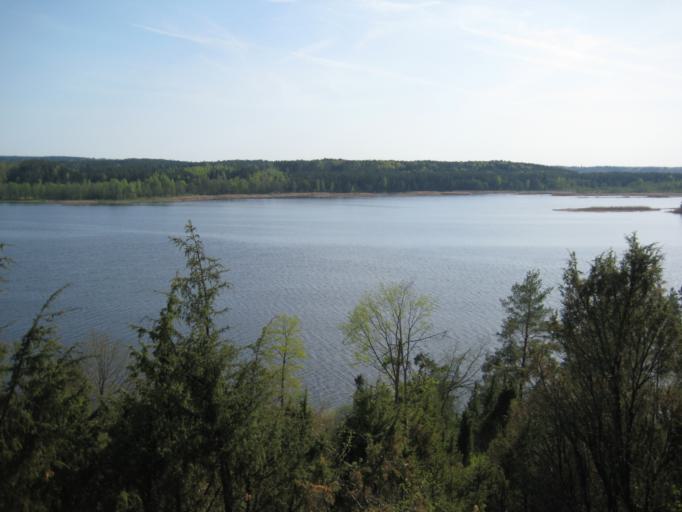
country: LT
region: Kauno apskritis
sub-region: Kauno rajonas
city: Karmelava
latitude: 54.8119
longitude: 24.1825
